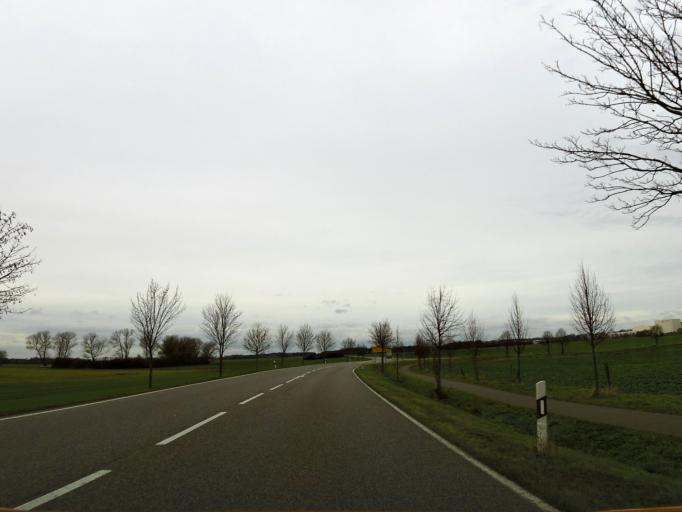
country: DE
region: Saxony-Anhalt
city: Pretzier
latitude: 52.8167
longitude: 11.2125
